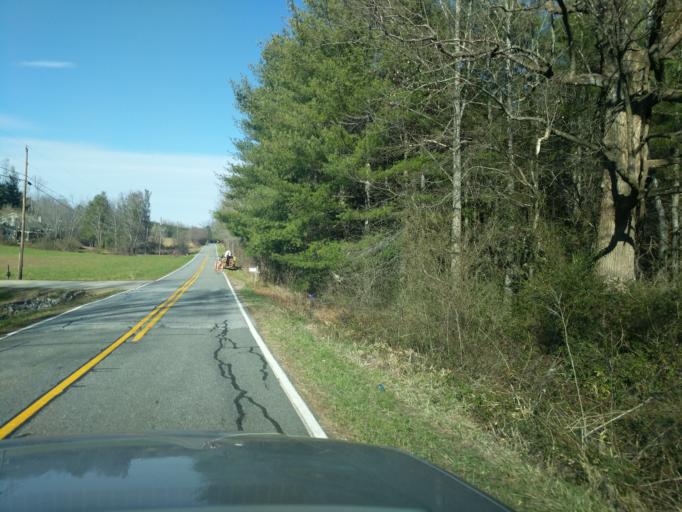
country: US
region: North Carolina
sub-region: McDowell County
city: West Marion
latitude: 35.5973
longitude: -81.9785
